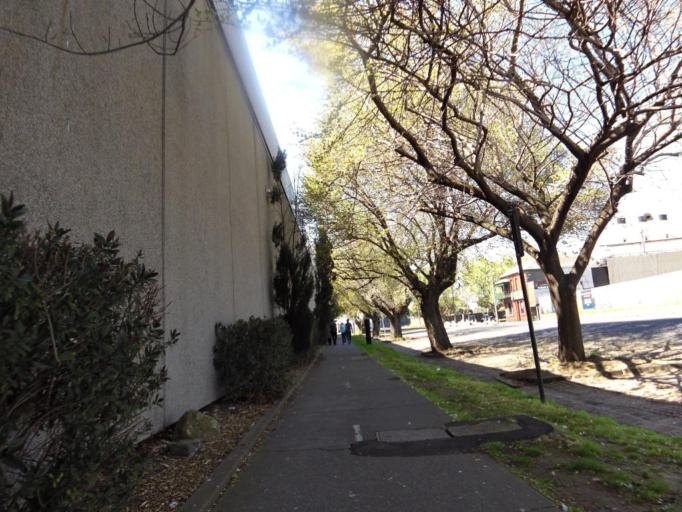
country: AU
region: Victoria
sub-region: Hobsons Bay
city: Williamstown
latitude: -37.8646
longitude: 144.9093
